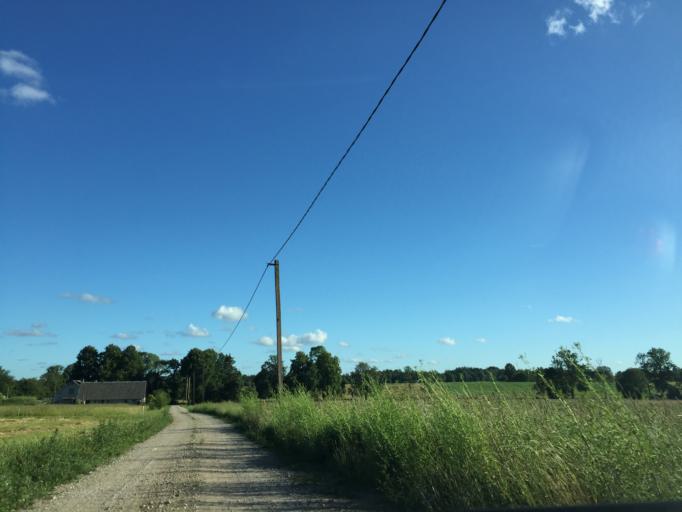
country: LV
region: Ventspils Rajons
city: Piltene
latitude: 57.4006
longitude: 21.8436
